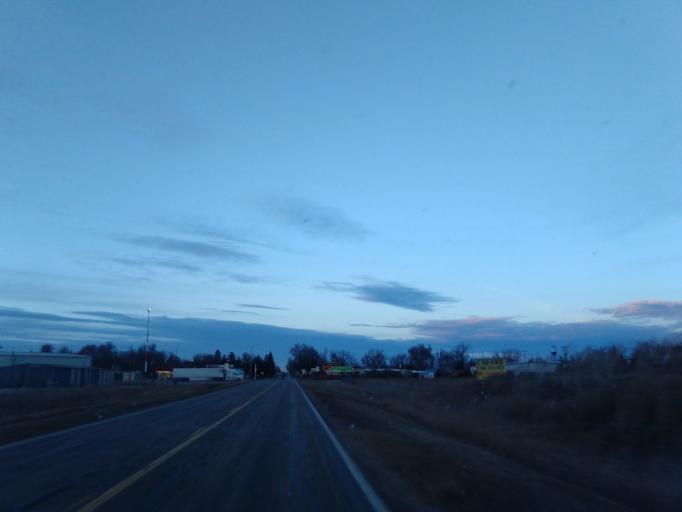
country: US
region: Nebraska
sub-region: Garden County
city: Oshkosh
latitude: 41.4001
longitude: -102.3475
